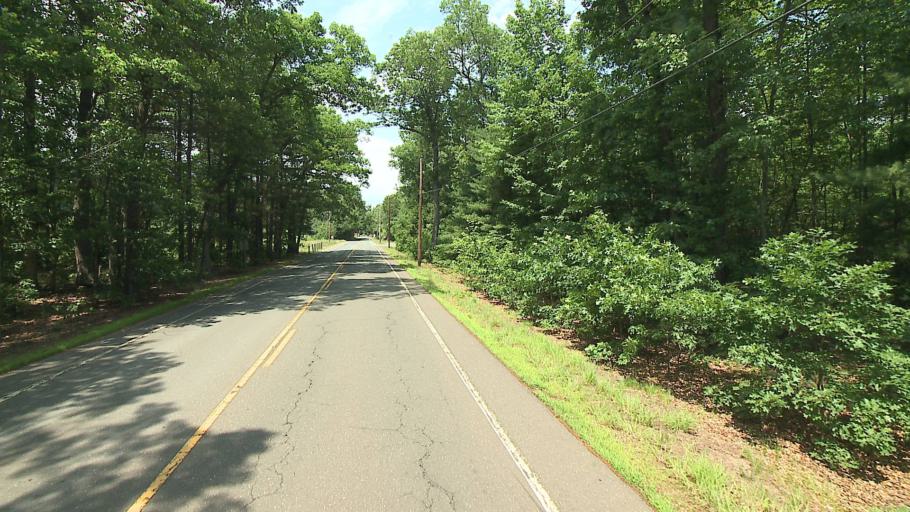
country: US
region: Massachusetts
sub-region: Hampden County
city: Southwick
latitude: 42.0349
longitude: -72.7506
